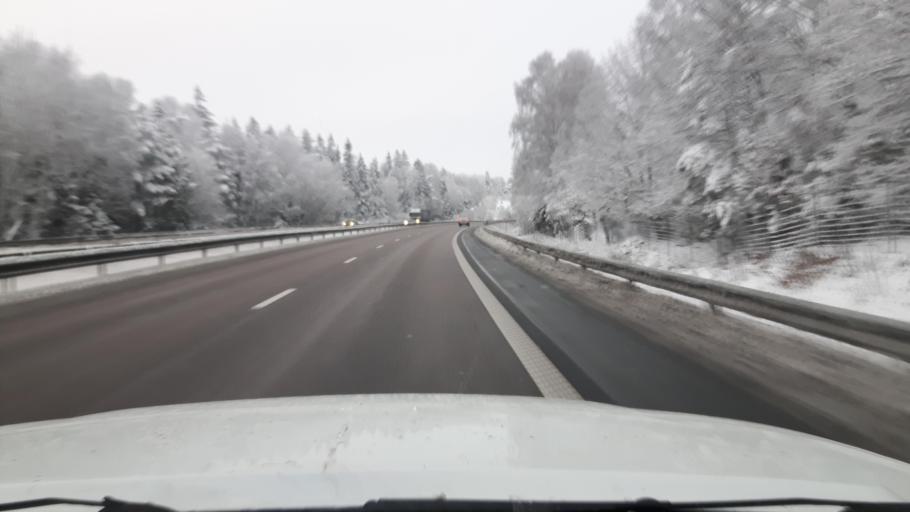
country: SE
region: Halland
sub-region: Kungsbacka Kommun
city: Kungsbacka
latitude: 57.4774
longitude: 12.0455
